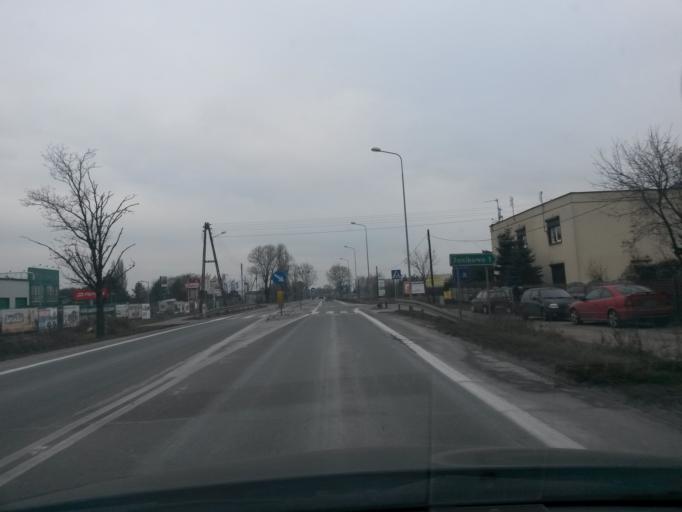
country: PL
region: Greater Poland Voivodeship
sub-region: Powiat poznanski
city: Kobylnica
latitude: 52.4382
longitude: 17.0379
